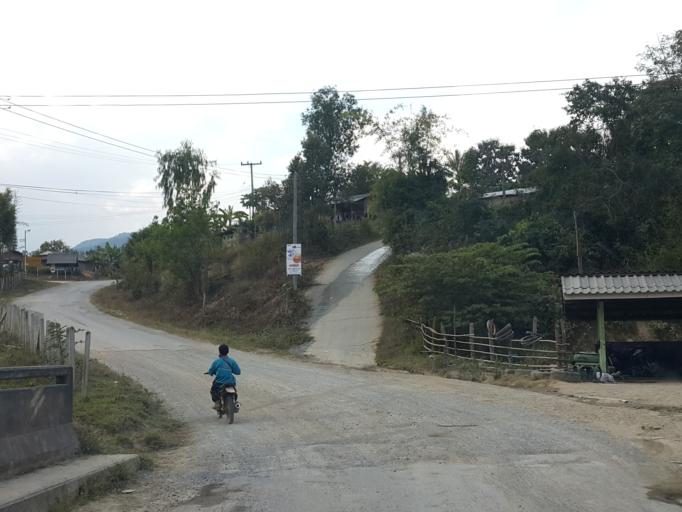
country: TH
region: Chiang Mai
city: Om Koi
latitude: 17.8013
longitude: 98.3356
